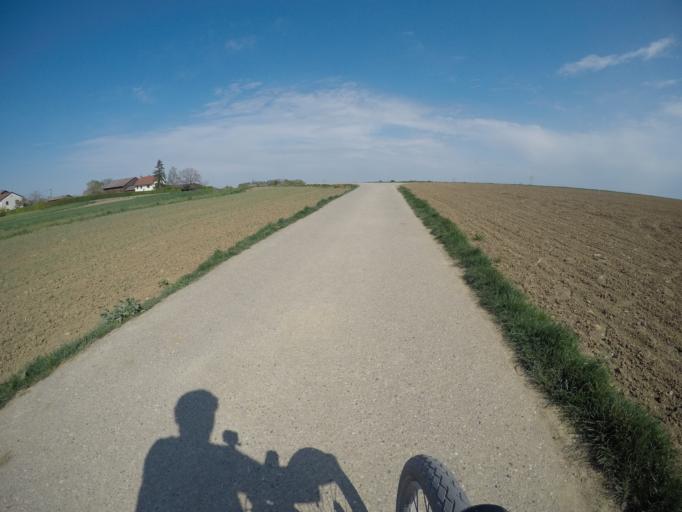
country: DE
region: Baden-Wuerttemberg
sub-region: Regierungsbezirk Stuttgart
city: Ditzingen
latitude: 48.8343
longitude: 9.0801
